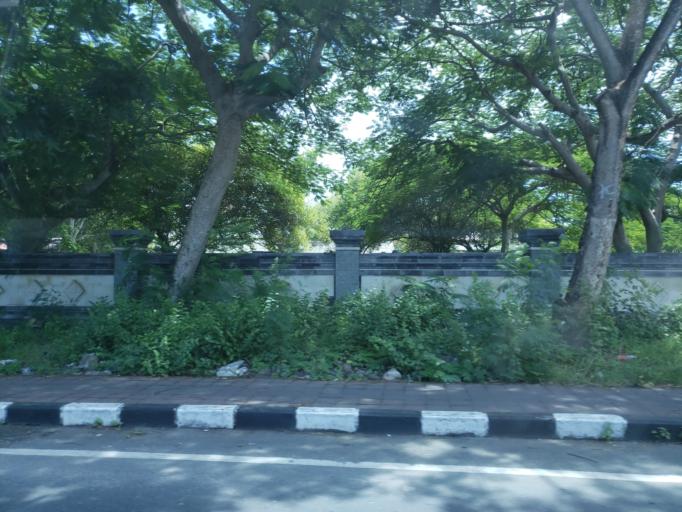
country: ID
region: Bali
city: Jimbaran
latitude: -8.8007
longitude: 115.1606
